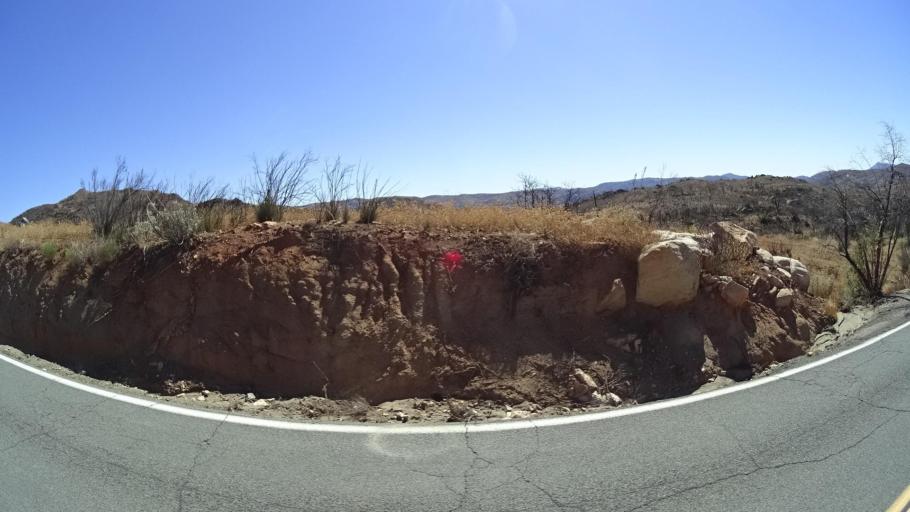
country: US
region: California
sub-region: San Diego County
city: Alpine
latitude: 32.7355
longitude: -116.6916
